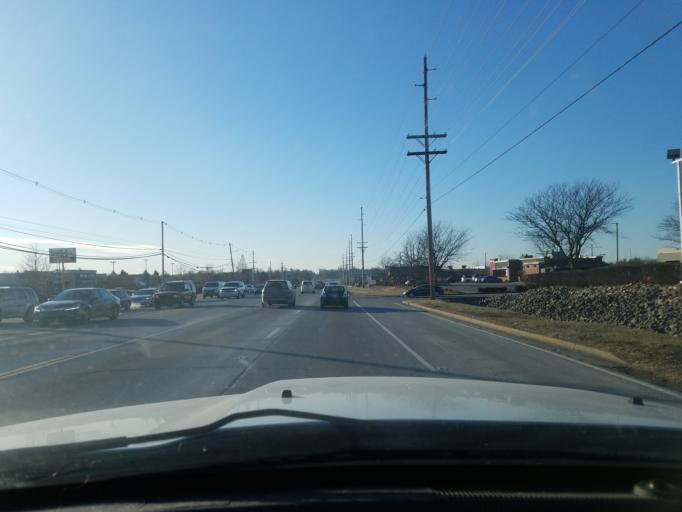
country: US
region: Kentucky
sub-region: Jefferson County
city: Middletown
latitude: 38.2429
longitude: -85.5115
